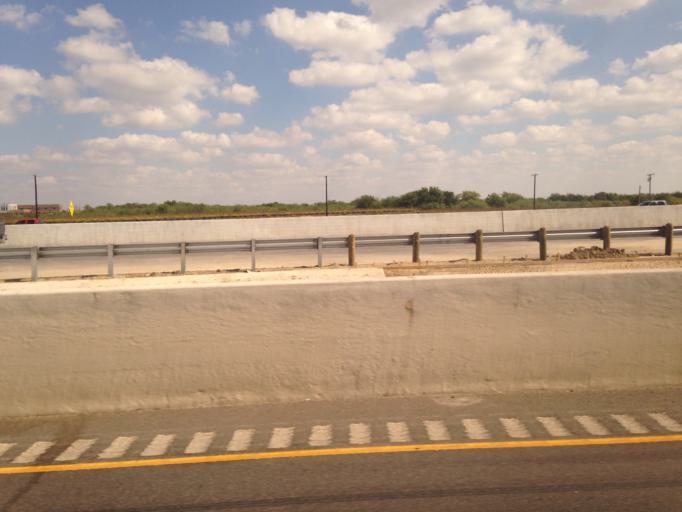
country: US
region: Texas
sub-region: Tarrant County
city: Blue Mound
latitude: 32.8882
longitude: -97.3175
